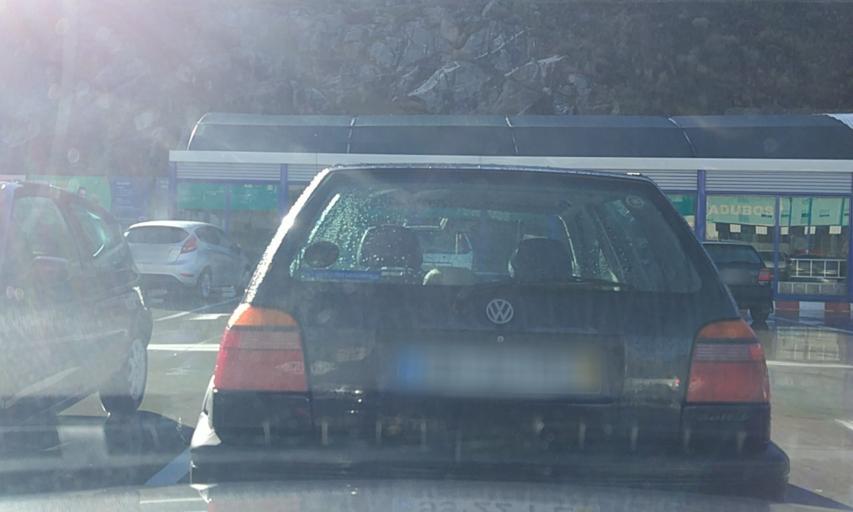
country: PT
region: Viseu
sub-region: Lamego
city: Lamego
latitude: 41.0885
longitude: -7.7991
